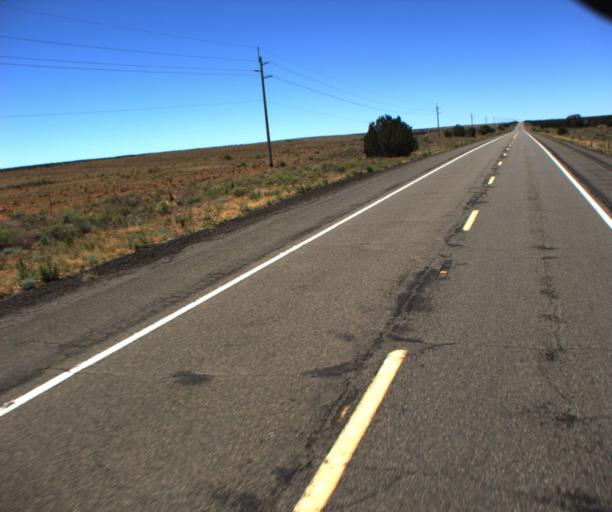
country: US
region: Arizona
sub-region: Coconino County
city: LeChee
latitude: 34.8192
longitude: -110.9632
